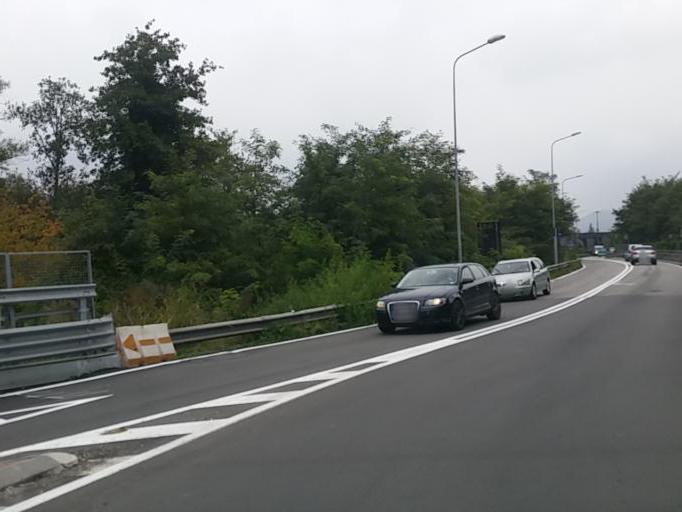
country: IT
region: Piedmont
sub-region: Provincia di Novara
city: Castelletto Sopra Ticino
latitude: 45.7199
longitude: 8.6258
